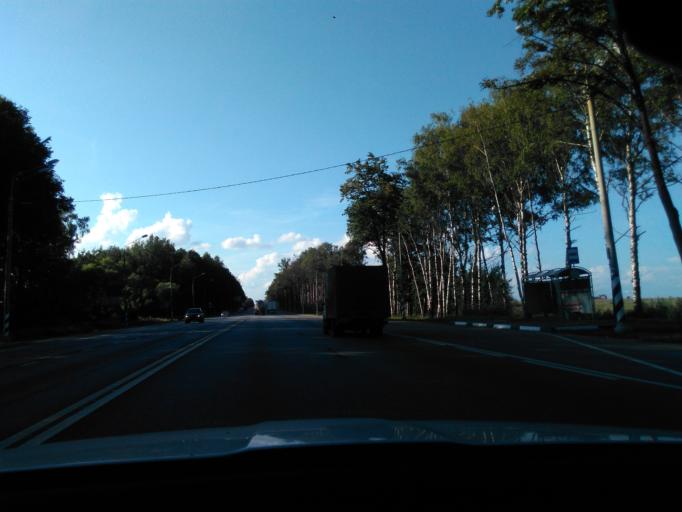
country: RU
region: Tverskaya
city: Zavidovo
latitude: 56.5565
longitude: 36.5106
